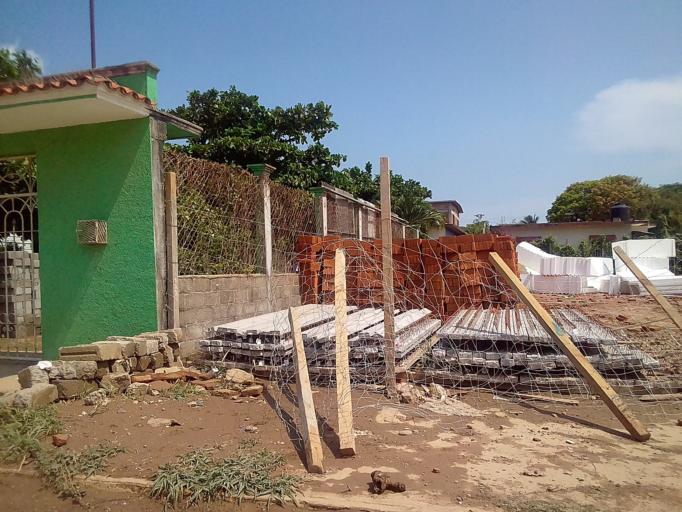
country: MX
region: Oaxaca
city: Union Hidalgo
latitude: 16.4700
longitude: -94.8315
